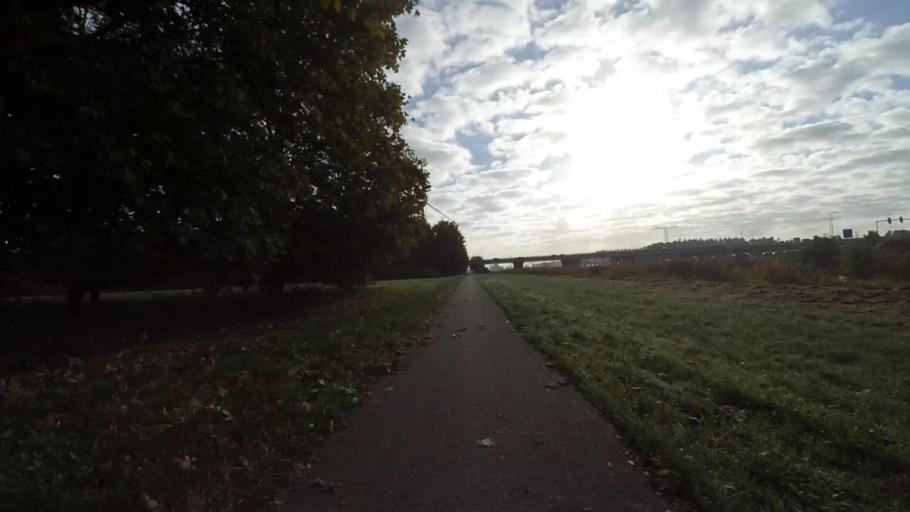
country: NL
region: Utrecht
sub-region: Gemeente Bunschoten
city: Spakenburg
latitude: 52.3162
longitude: 5.3304
